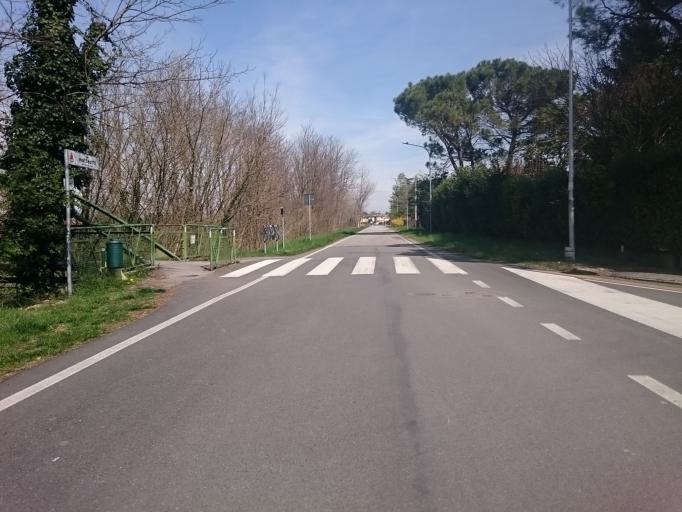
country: IT
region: Veneto
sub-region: Provincia di Padova
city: Limena
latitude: 45.4750
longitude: 11.8398
